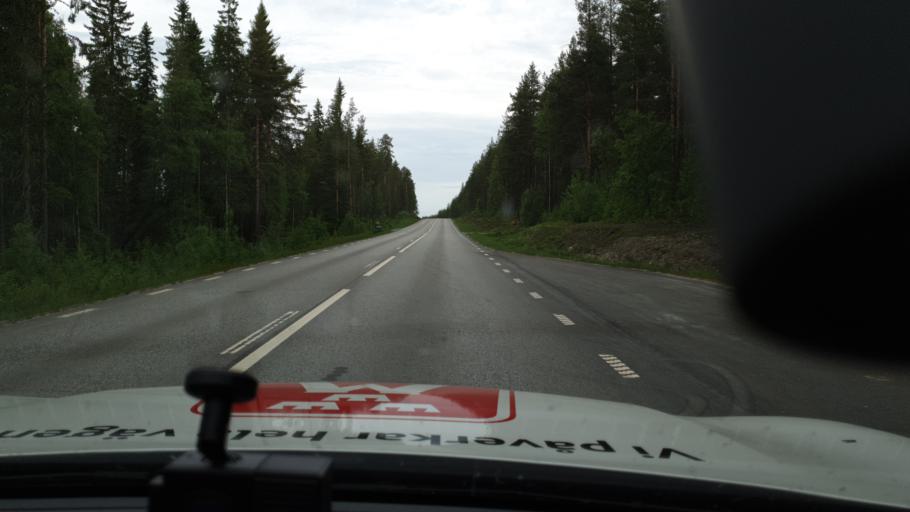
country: SE
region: Vaesterbotten
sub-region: Lycksele Kommun
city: Lycksele
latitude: 64.5543
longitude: 18.7324
